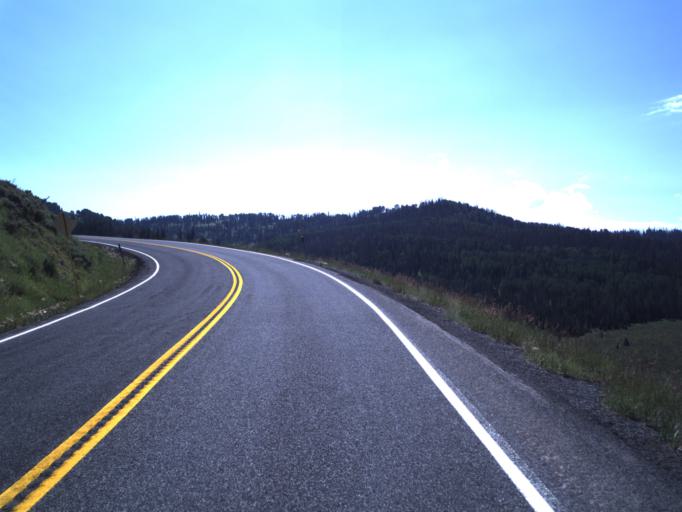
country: US
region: Utah
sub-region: Sanpete County
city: Fairview
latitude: 39.6843
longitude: -111.2436
